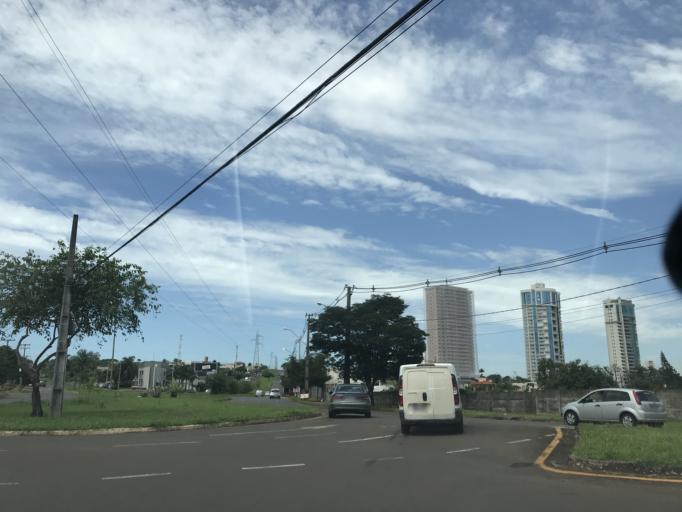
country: BR
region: Parana
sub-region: Londrina
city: Londrina
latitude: -23.3424
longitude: -51.1593
